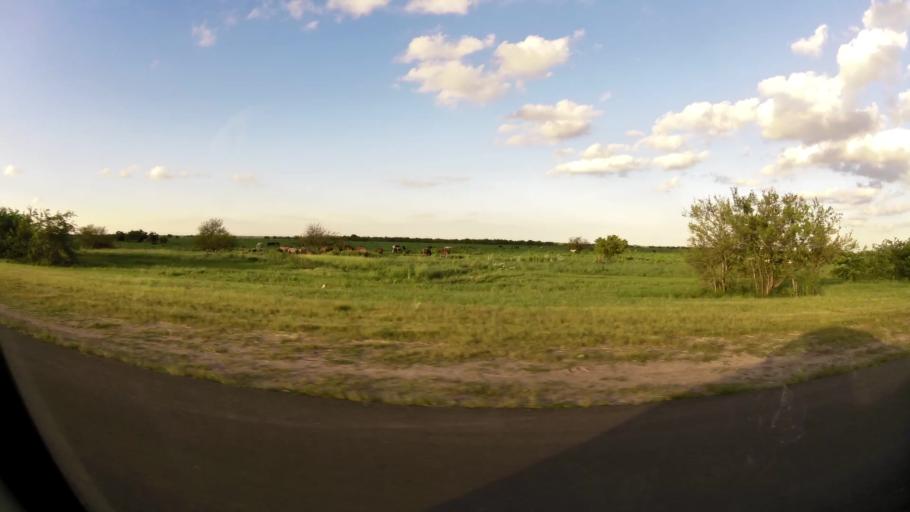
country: AR
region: Buenos Aires
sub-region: Partido de La Plata
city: La Plata
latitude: -34.8574
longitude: -58.0279
